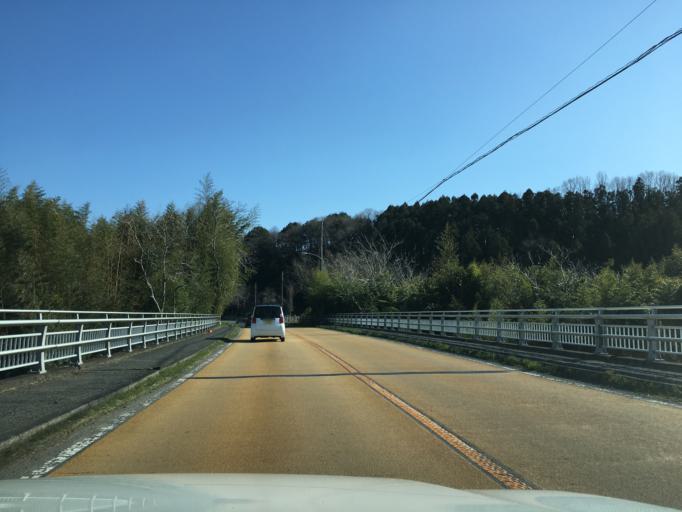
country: JP
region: Ibaraki
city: Mito-shi
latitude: 36.4426
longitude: 140.4121
